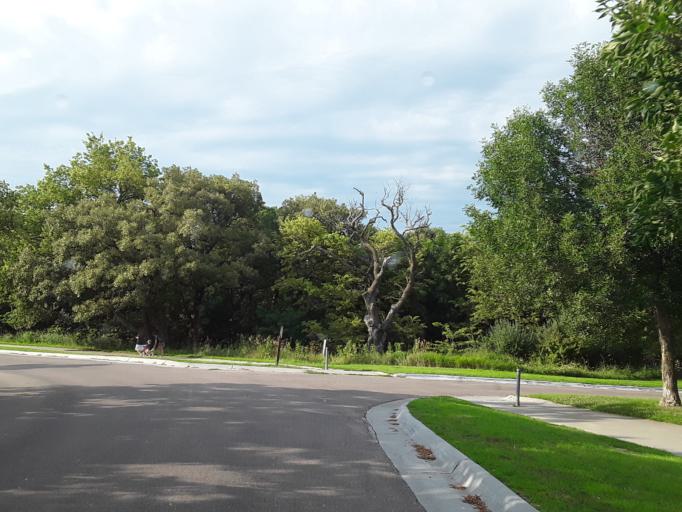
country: US
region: Nebraska
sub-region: Saunders County
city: Ashland
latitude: 41.0311
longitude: -96.3118
